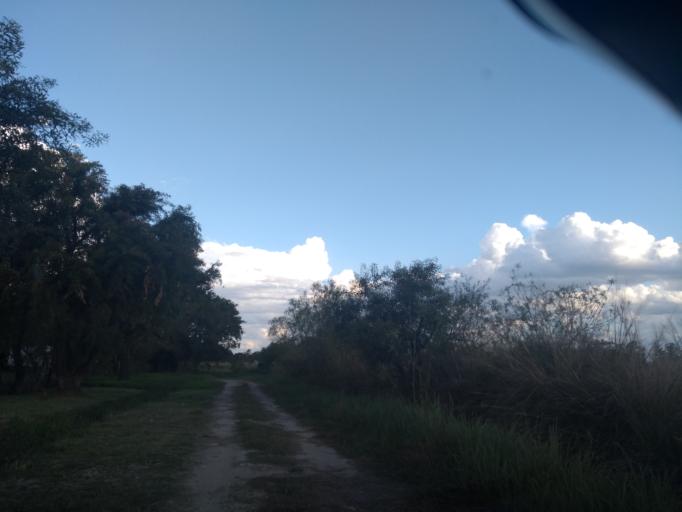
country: AR
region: Chaco
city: Resistencia
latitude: -27.4179
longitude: -58.9487
